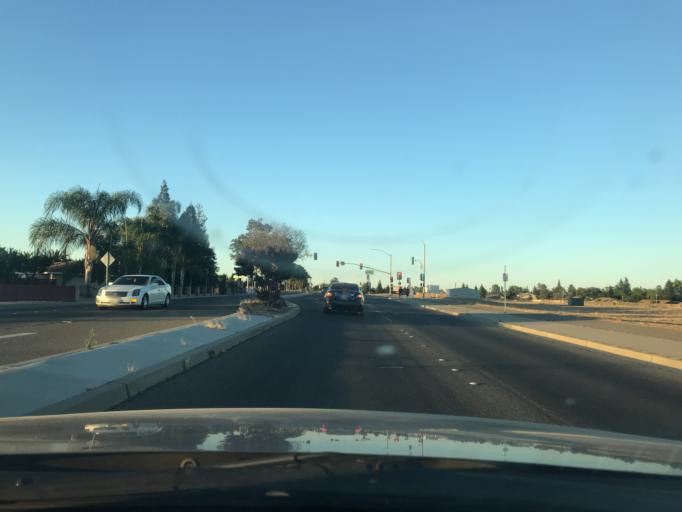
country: US
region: California
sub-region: Merced County
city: Atwater
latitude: 37.3506
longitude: -120.5768
